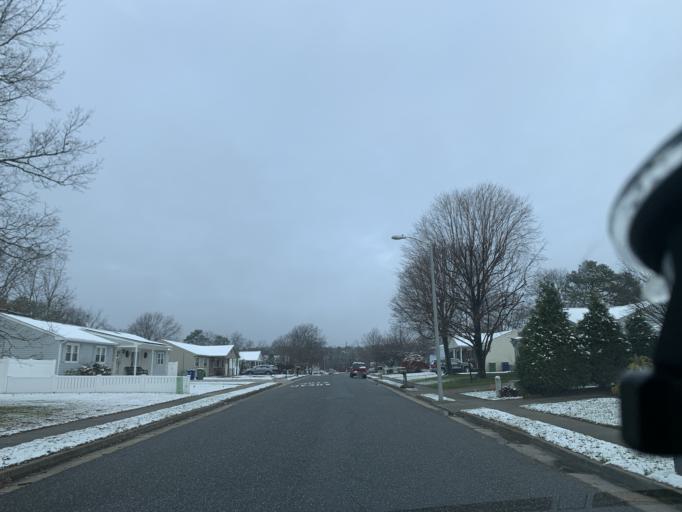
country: US
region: New Jersey
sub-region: Atlantic County
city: Pomona
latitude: 39.4325
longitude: -74.5912
